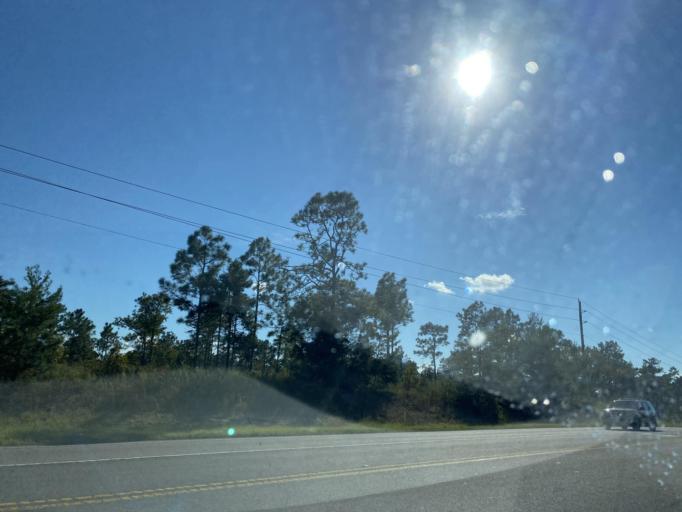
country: US
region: Florida
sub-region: Marion County
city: Ocala
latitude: 29.0522
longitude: -82.2616
